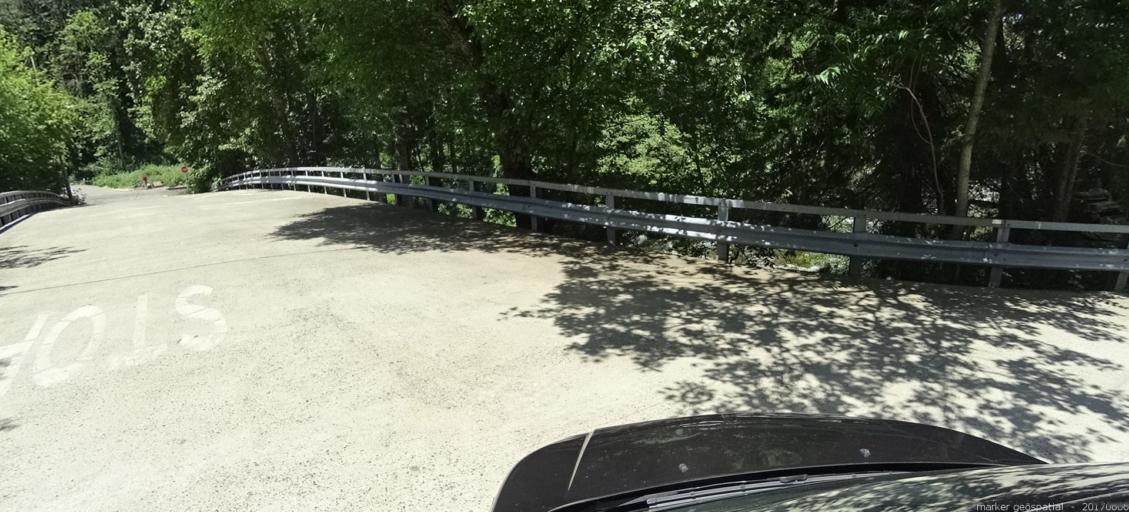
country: US
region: California
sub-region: Siskiyou County
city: Dunsmuir
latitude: 41.2175
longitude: -122.2715
